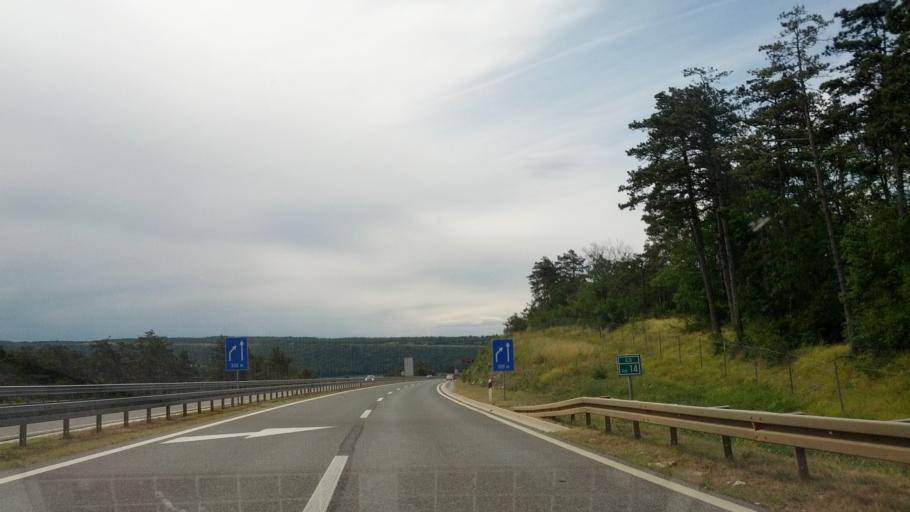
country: HR
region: Istarska
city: Novigrad
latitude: 45.3484
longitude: 13.6209
